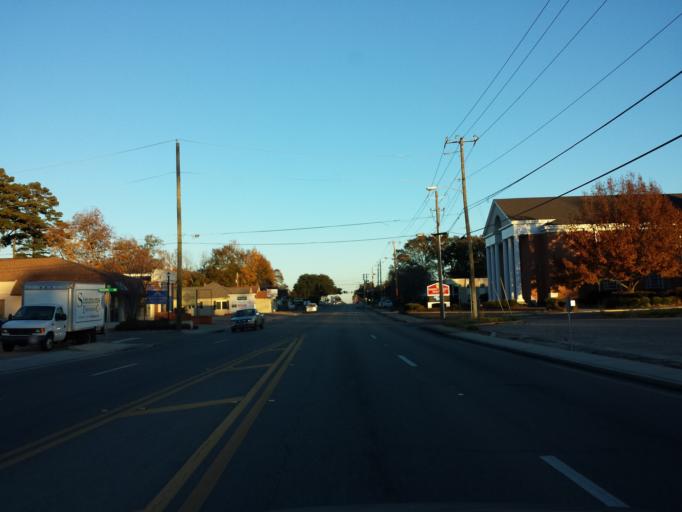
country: US
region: Mississippi
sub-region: Forrest County
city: Hattiesburg
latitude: 31.3247
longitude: -89.3135
